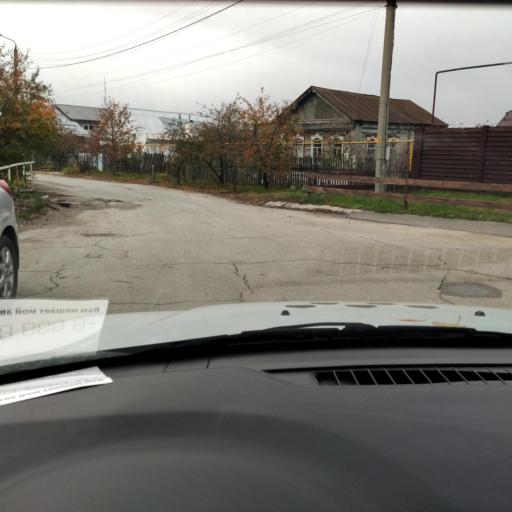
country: RU
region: Samara
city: Tol'yatti
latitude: 53.5277
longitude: 49.4064
